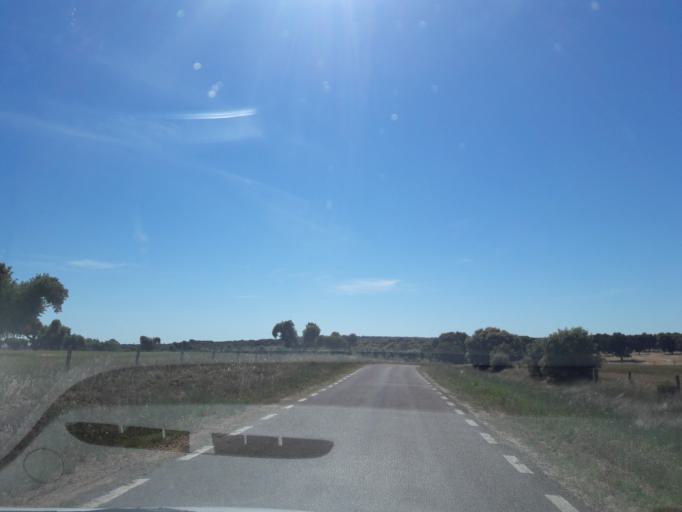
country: ES
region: Castille and Leon
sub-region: Provincia de Salamanca
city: Zarapicos
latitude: 41.0228
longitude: -5.8280
